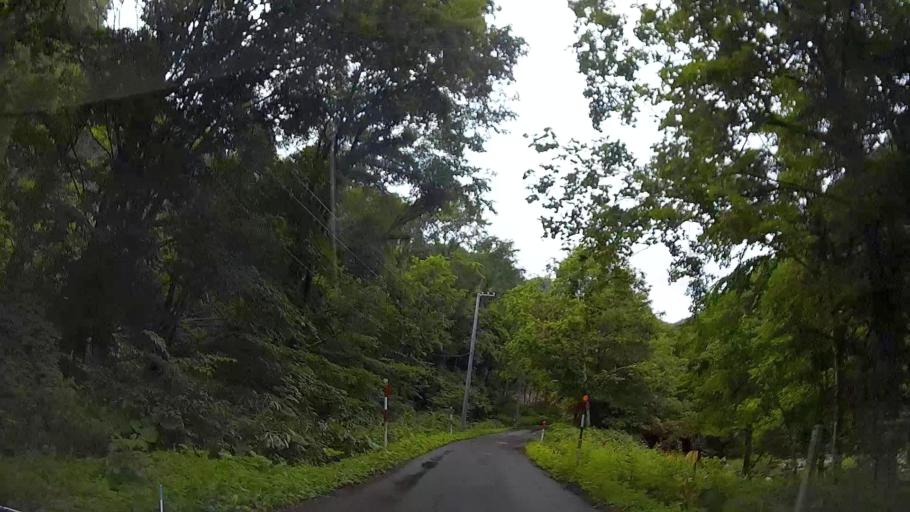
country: JP
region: Hokkaido
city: Nanae
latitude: 42.0749
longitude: 140.5291
